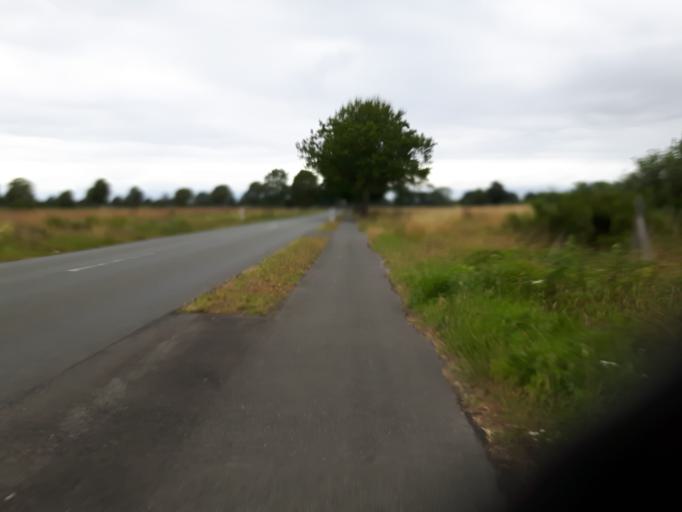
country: DE
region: Lower Saxony
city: Stuhr
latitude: 53.0077
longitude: 8.7701
